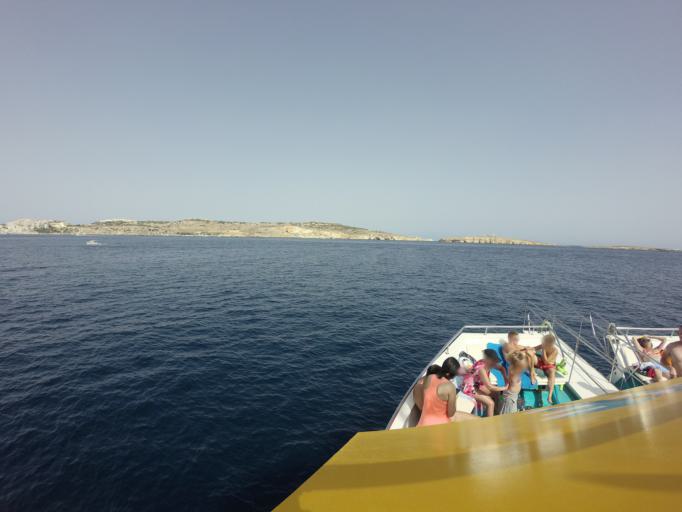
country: MT
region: Saint Paul's Bay
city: San Pawl il-Bahar
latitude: 35.9553
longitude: 14.4052
